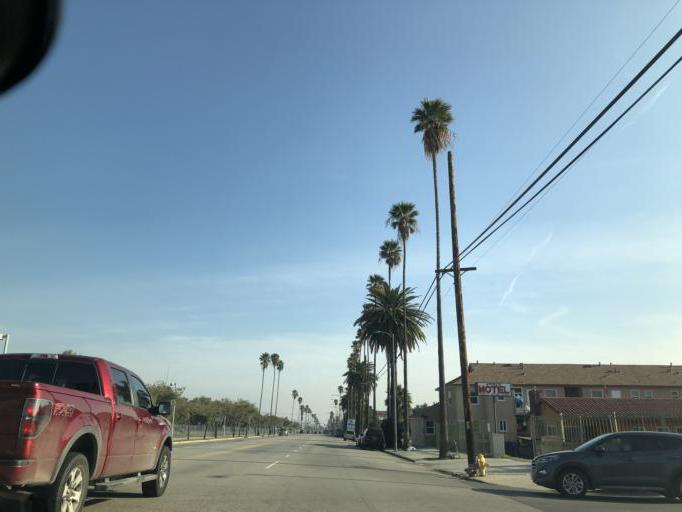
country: US
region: California
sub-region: Los Angeles County
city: San Fernando
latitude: 34.3071
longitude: -118.4696
